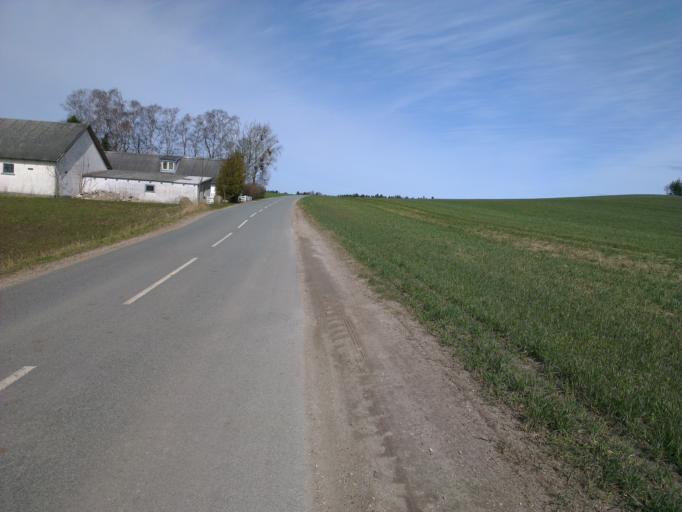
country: DK
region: Capital Region
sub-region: Egedal Kommune
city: Olstykke
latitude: 55.8432
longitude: 12.1255
